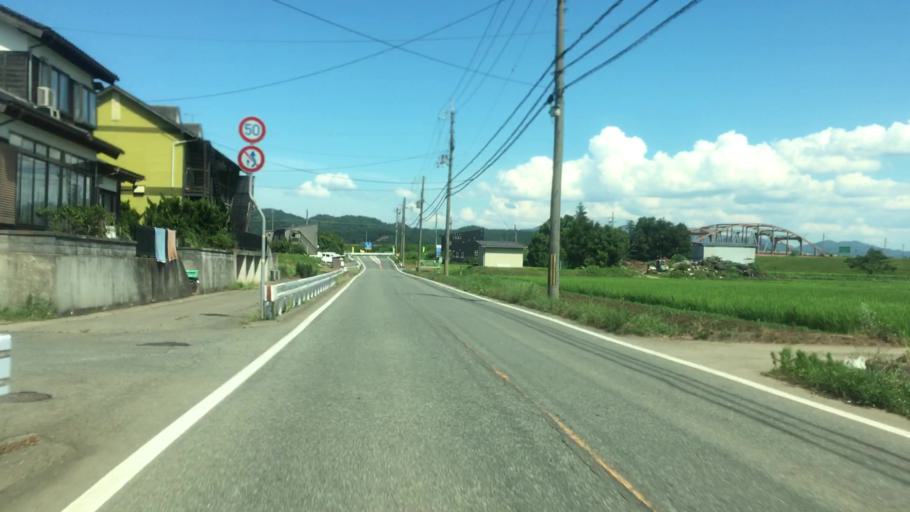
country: JP
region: Hyogo
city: Toyooka
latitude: 35.5659
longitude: 134.8006
